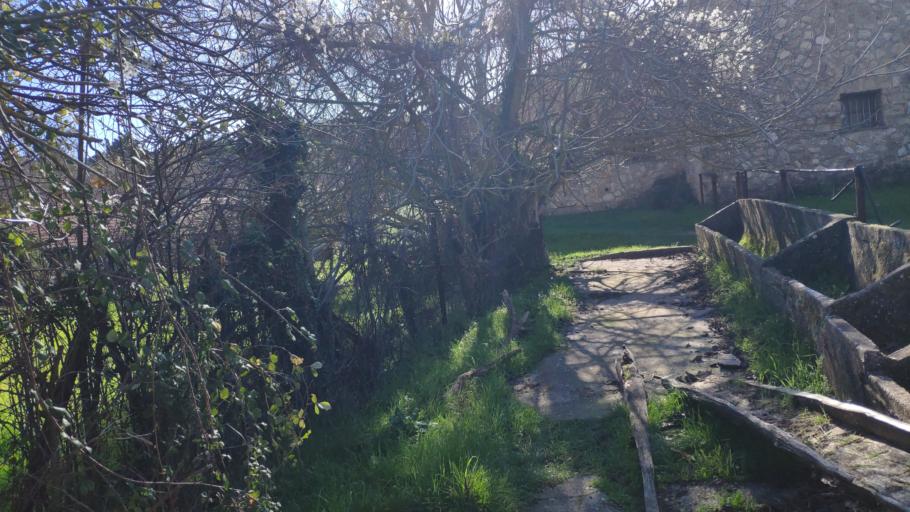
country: GR
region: Attica
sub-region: Nomarchia Anatolikis Attikis
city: Varybobi
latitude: 38.1564
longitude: 23.7960
